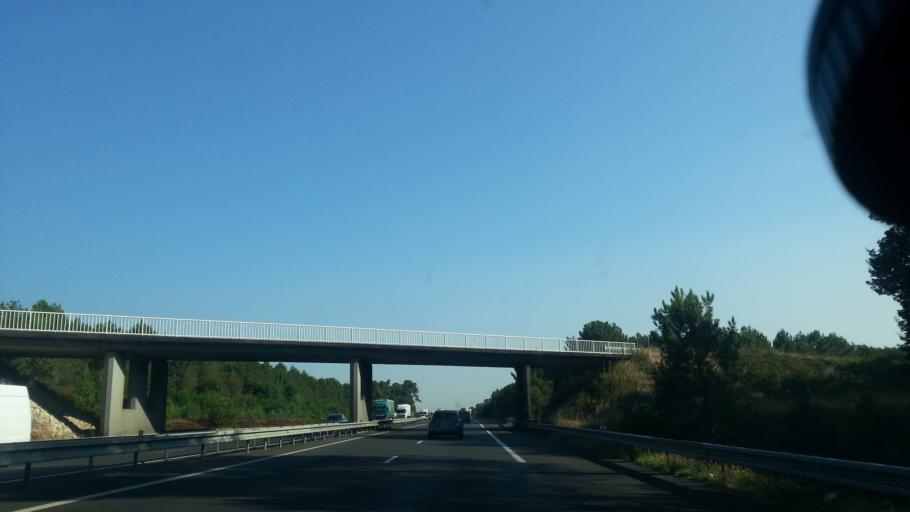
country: FR
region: Poitou-Charentes
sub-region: Departement de la Vienne
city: Chatellerault
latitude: 46.8017
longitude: 0.5130
